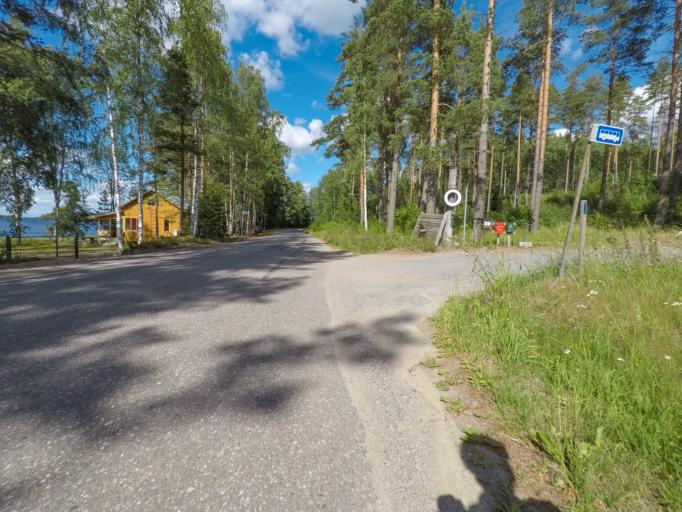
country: FI
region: South Karelia
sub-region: Lappeenranta
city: Joutseno
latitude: 61.1168
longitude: 28.3749
